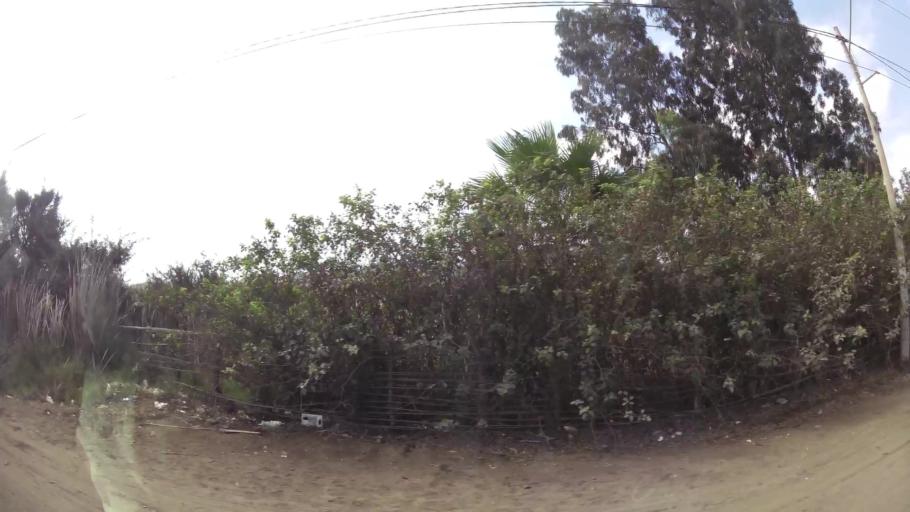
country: PE
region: Lima
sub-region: Provincia de Canete
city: Mala
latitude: -12.6940
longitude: -76.6246
